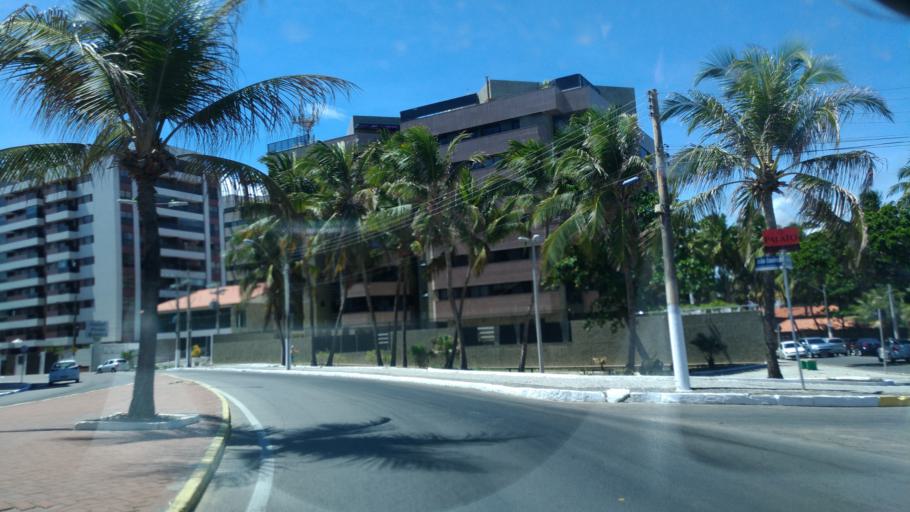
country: BR
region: Alagoas
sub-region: Maceio
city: Maceio
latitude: -9.6437
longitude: -35.6993
